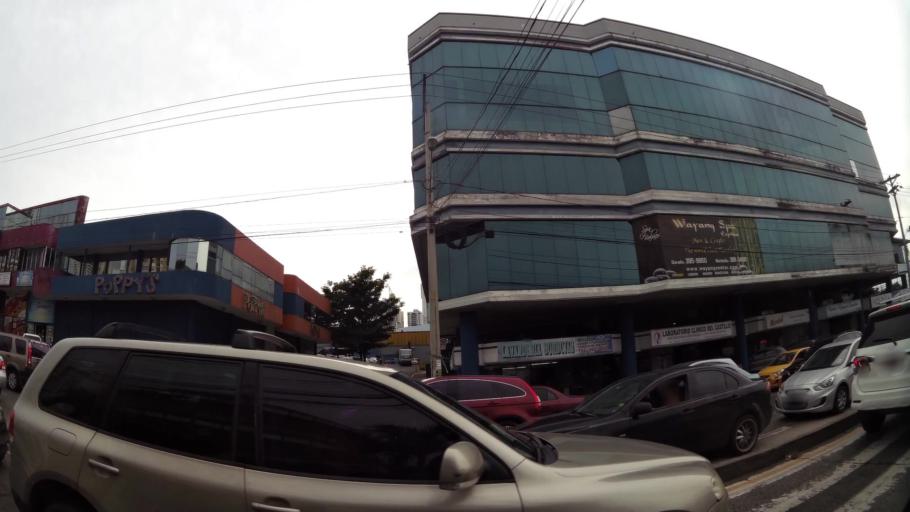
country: PA
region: Panama
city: Panama
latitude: 9.0107
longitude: -79.5365
